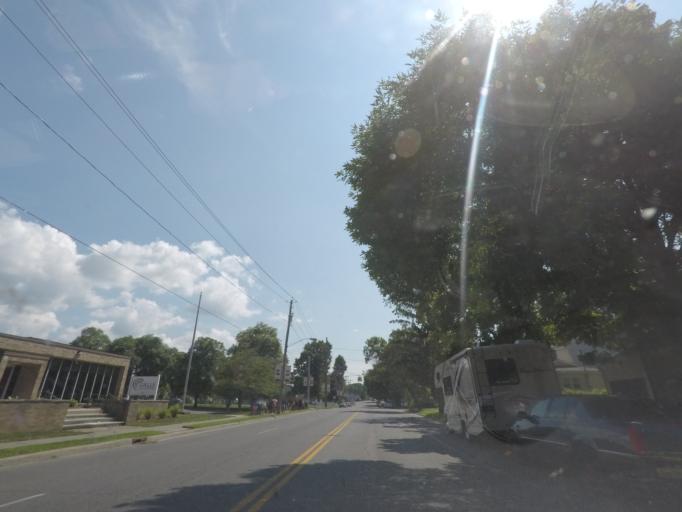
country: US
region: New York
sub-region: Albany County
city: Watervliet
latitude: 42.7255
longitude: -73.7027
